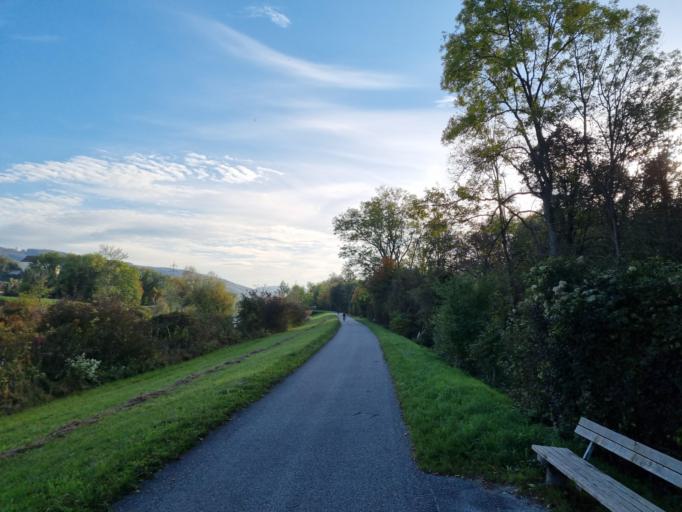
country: AT
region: Lower Austria
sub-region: Politischer Bezirk Sankt Polten
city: Wilhelmsburg
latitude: 48.1371
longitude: 15.6336
